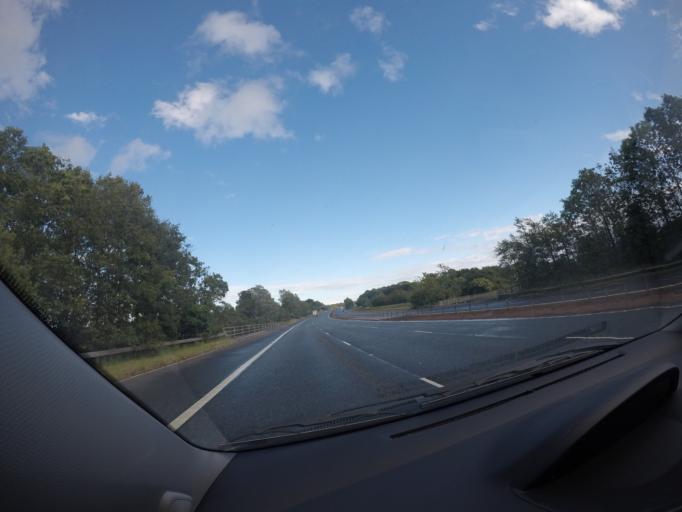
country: GB
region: Scotland
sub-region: Dumfries and Galloway
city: Annan
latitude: 55.0459
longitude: -3.1921
